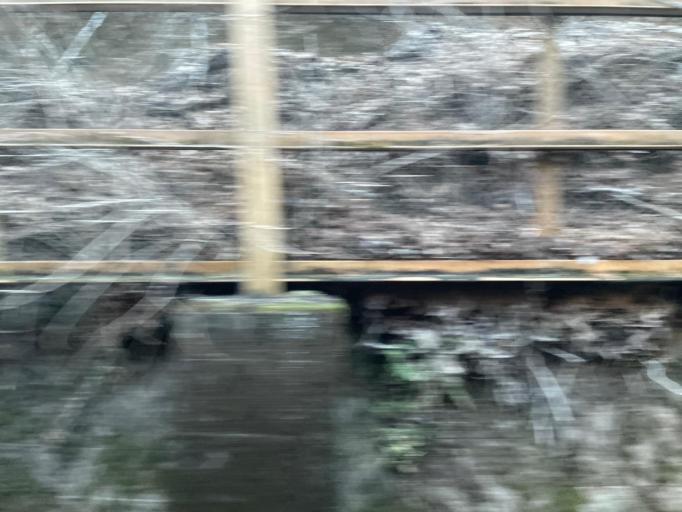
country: JP
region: Ibaraki
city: Daigo
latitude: 36.6844
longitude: 140.3899
